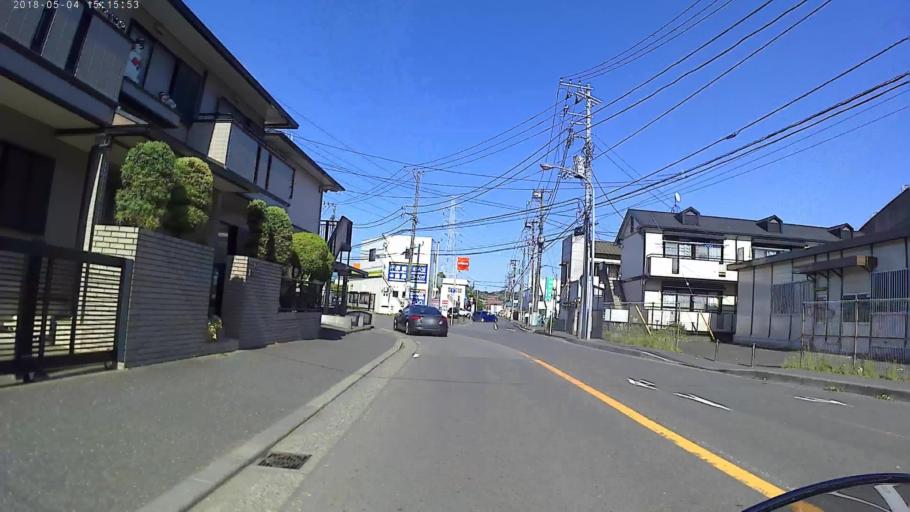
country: JP
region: Kanagawa
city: Yokohama
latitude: 35.5309
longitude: 139.6095
